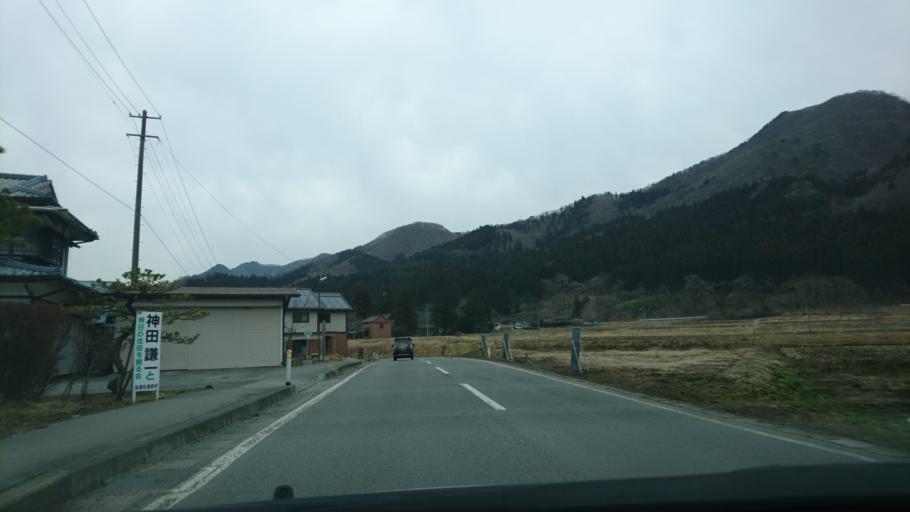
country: JP
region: Iwate
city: Tono
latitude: 39.2019
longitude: 141.5909
